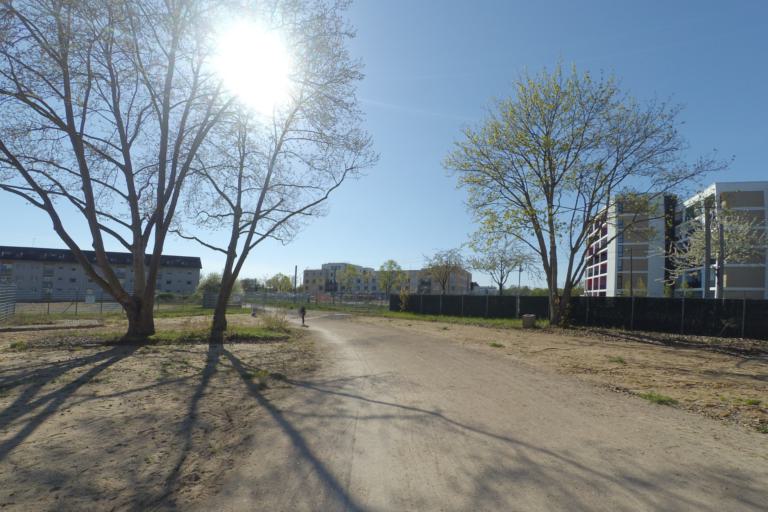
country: DE
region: Baden-Wuerttemberg
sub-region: Karlsruhe Region
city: Mannheim
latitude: 49.5144
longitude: 8.5294
